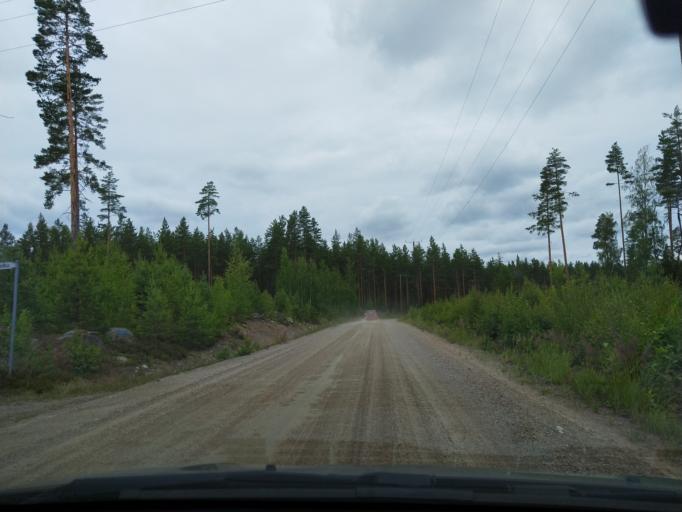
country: FI
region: Southern Savonia
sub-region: Mikkeli
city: Maentyharju
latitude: 61.1328
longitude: 26.8903
